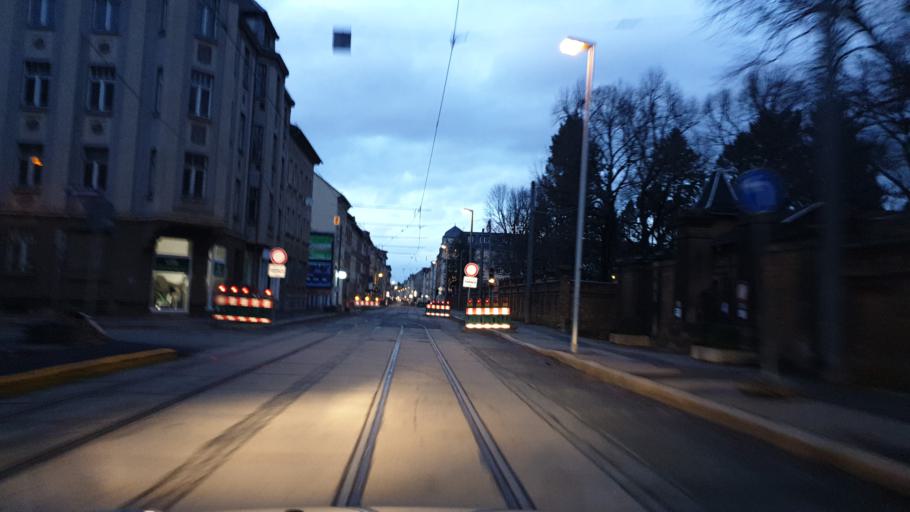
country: DE
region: Thuringia
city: Gera
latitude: 50.8614
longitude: 12.0729
